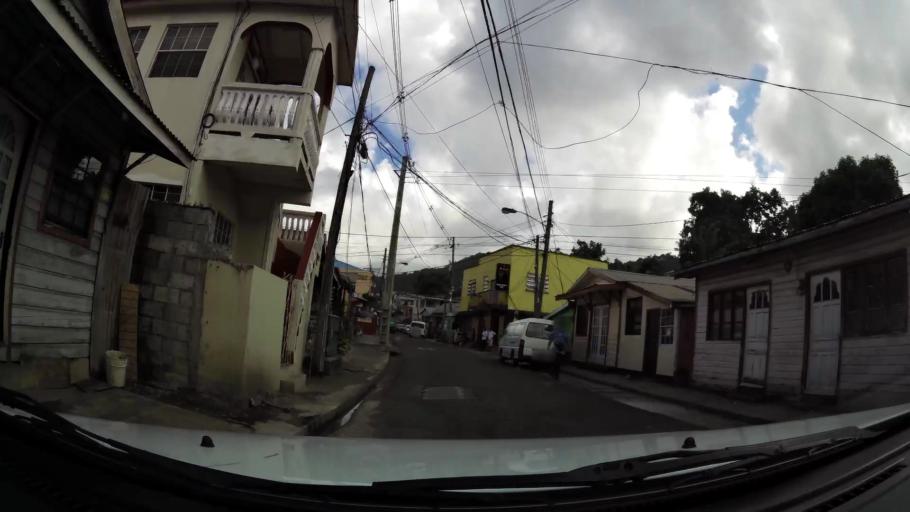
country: LC
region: Castries Quarter
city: Castries
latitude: 14.0044
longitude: -60.9869
